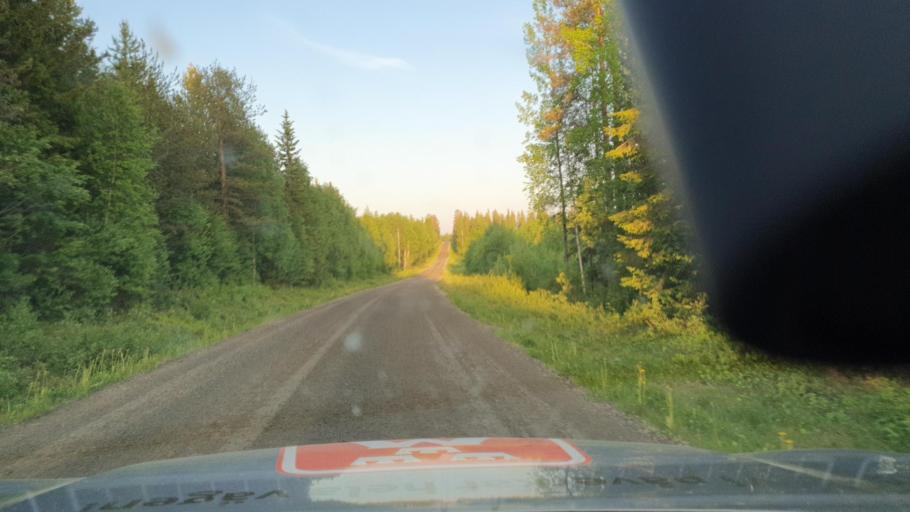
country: SE
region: Norrbotten
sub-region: Bodens Kommun
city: Boden
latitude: 66.0626
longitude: 21.7289
